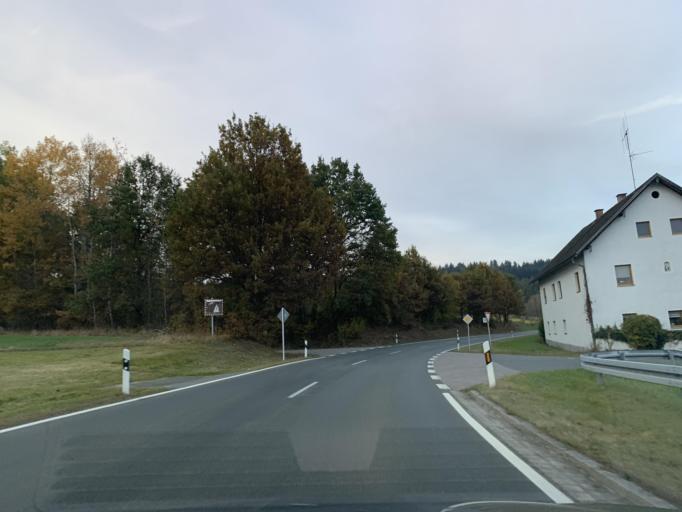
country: DE
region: Bavaria
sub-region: Upper Palatinate
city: Bach
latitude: 49.3775
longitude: 12.3757
